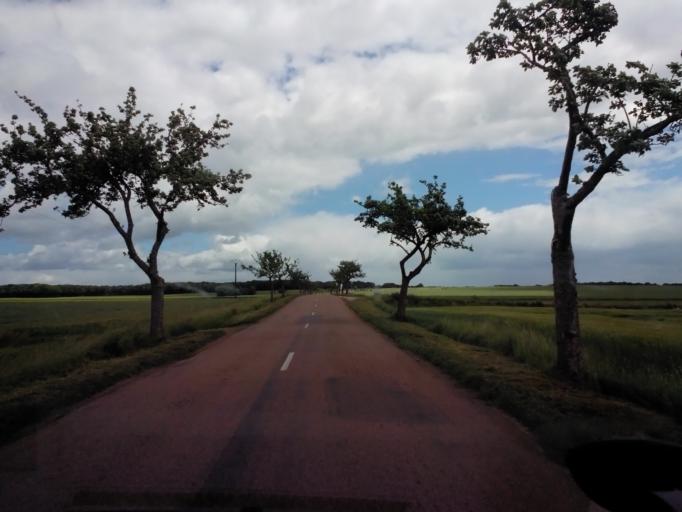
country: FR
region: Champagne-Ardenne
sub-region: Departement de la Haute-Marne
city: Rolampont
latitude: 47.9061
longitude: 5.2590
